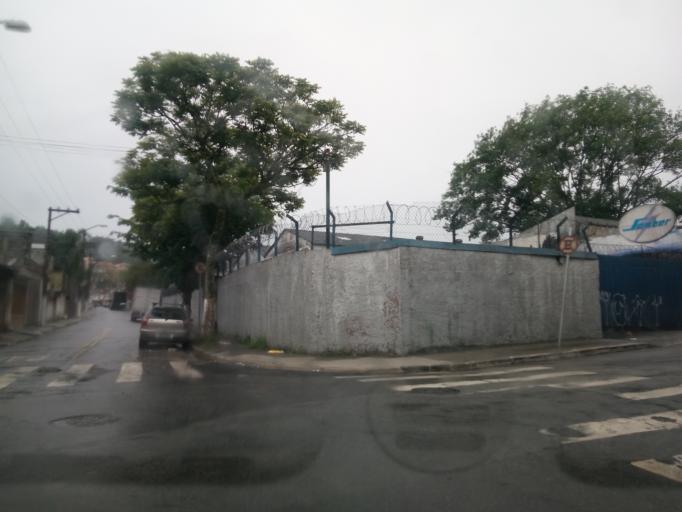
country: BR
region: Sao Paulo
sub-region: Sao Bernardo Do Campo
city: Sao Bernardo do Campo
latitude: -23.7339
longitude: -46.5391
